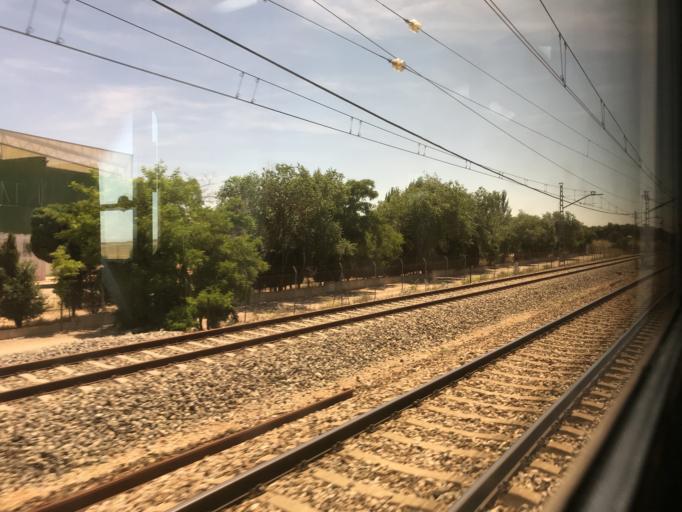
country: ES
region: Madrid
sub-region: Provincia de Madrid
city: Pinto
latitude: 40.2330
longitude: -3.6985
